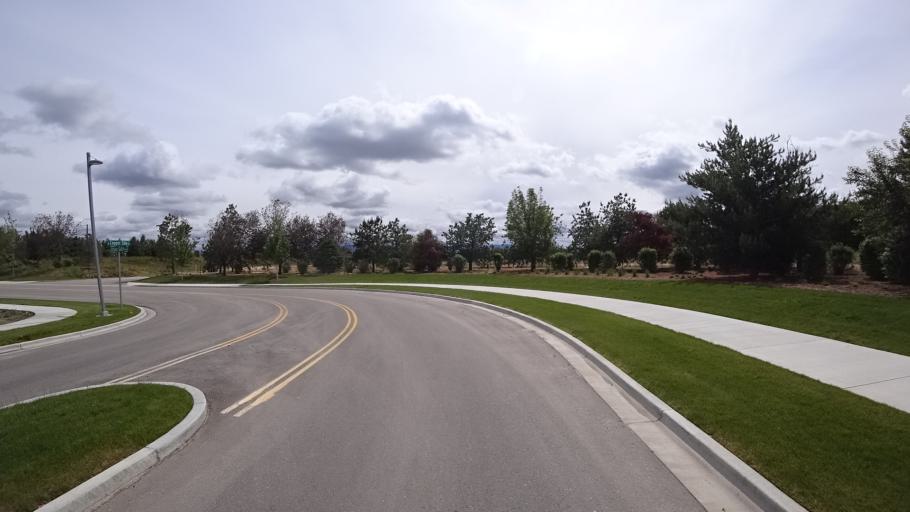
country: US
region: Idaho
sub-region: Ada County
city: Eagle
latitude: 43.6944
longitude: -116.3827
